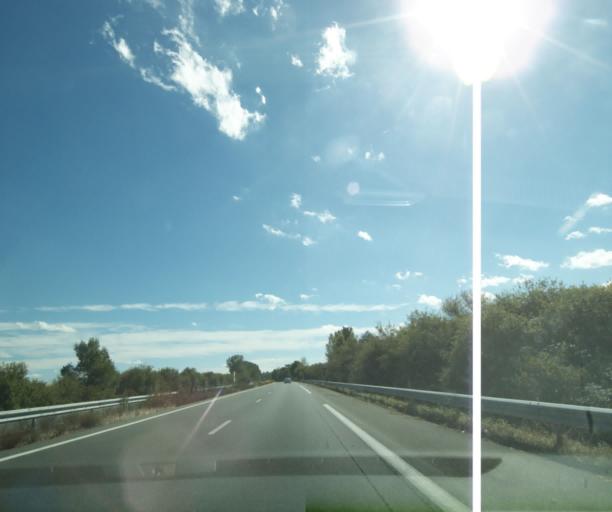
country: FR
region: Aquitaine
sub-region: Departement du Lot-et-Garonne
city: Damazan
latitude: 44.2924
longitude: 0.2625
